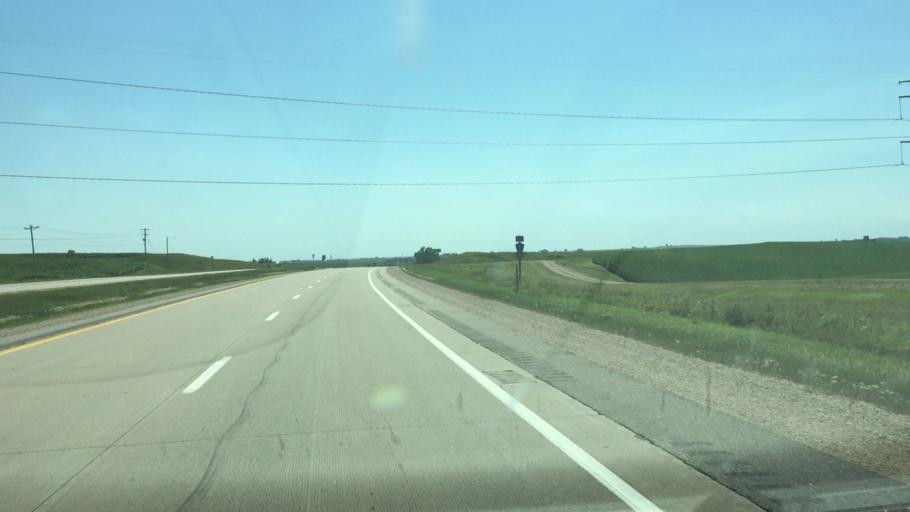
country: US
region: Iowa
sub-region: Dubuque County
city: Peosta
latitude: 42.3646
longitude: -90.8004
